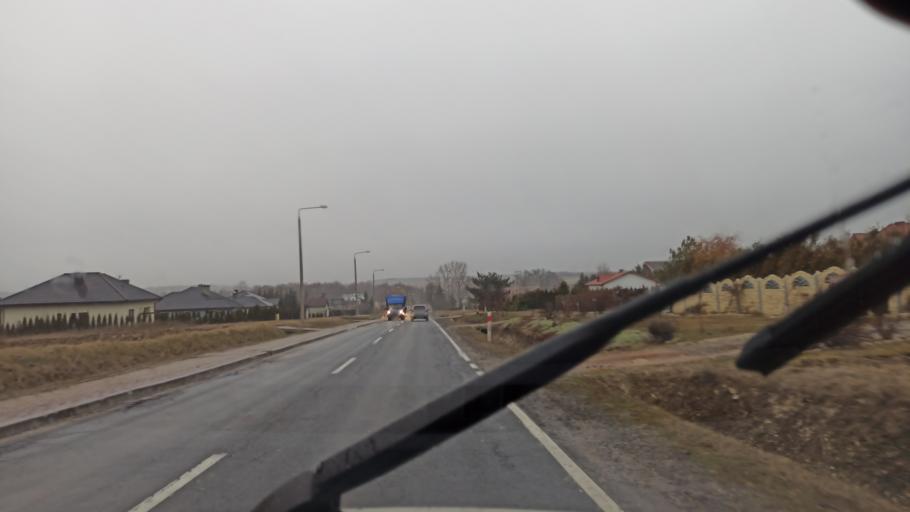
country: PL
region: Lublin Voivodeship
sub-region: Powiat lubelski
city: Strzyzowice
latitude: 51.0474
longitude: 22.4542
